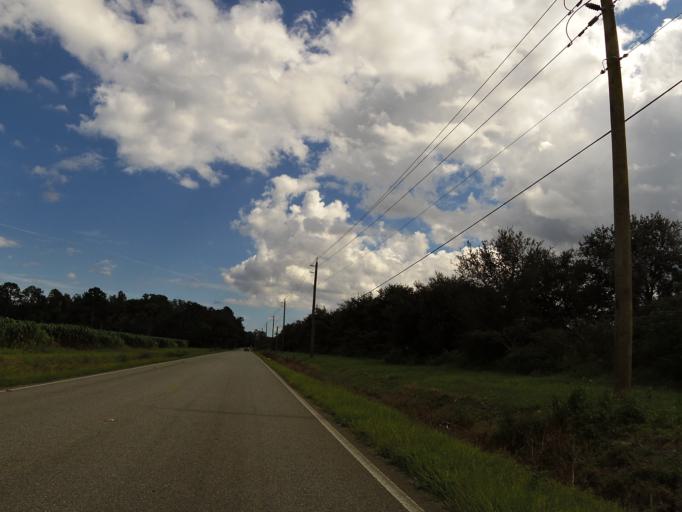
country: US
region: Florida
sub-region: Saint Johns County
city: Saint Augustine South
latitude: 29.8232
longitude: -81.4896
